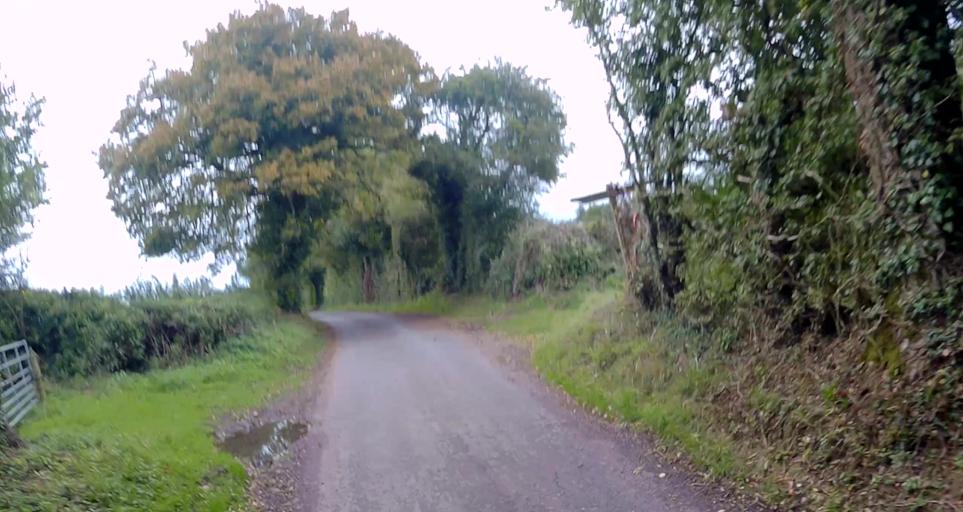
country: GB
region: England
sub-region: Hampshire
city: Four Marks
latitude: 51.1568
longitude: -1.0867
